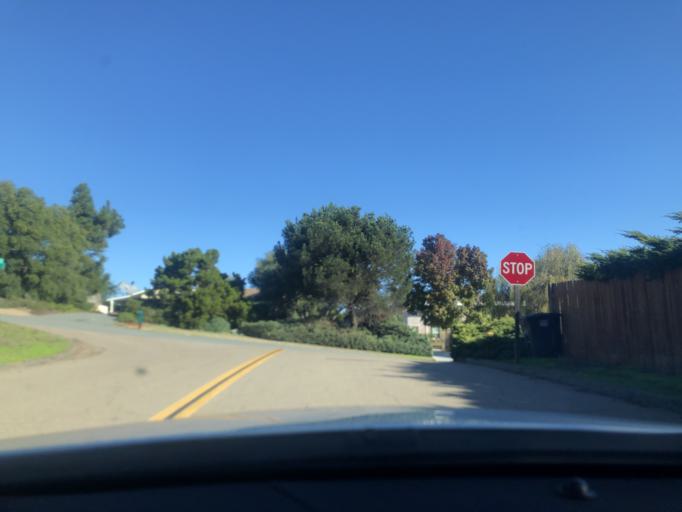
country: US
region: California
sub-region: San Diego County
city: Casa de Oro-Mount Helix
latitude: 32.7704
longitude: -116.9489
